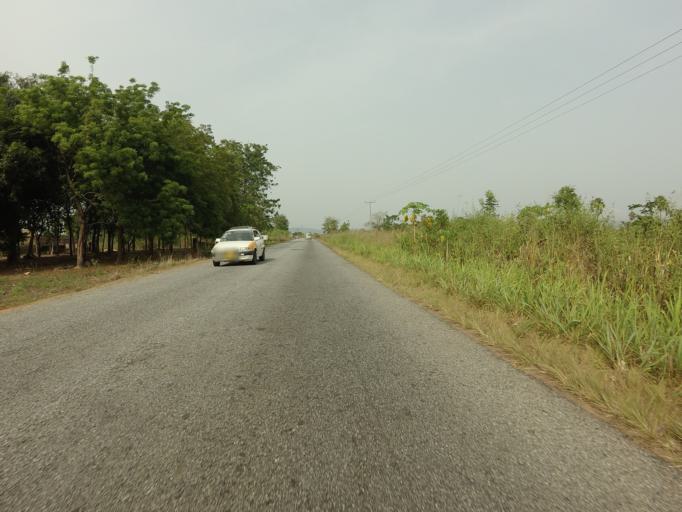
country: GH
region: Volta
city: Ho
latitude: 6.5731
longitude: 0.3613
